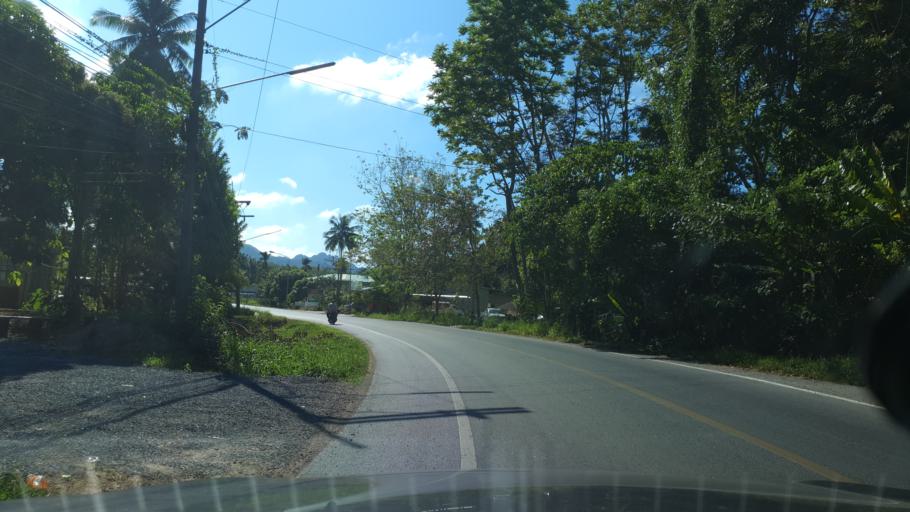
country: TH
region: Phangnga
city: Ban Ao Nang
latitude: 8.0657
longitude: 98.8093
